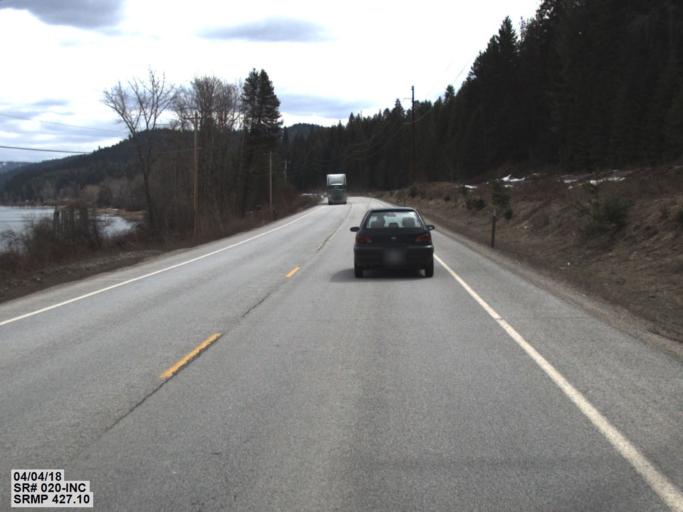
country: US
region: Washington
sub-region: Pend Oreille County
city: Newport
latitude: 48.2356
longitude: -117.2232
